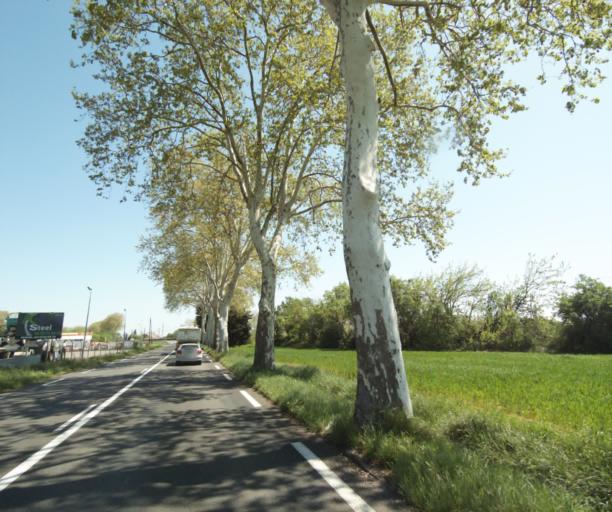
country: FR
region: Languedoc-Roussillon
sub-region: Departement de l'Herault
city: Saint-Bres
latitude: 43.6608
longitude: 4.0262
